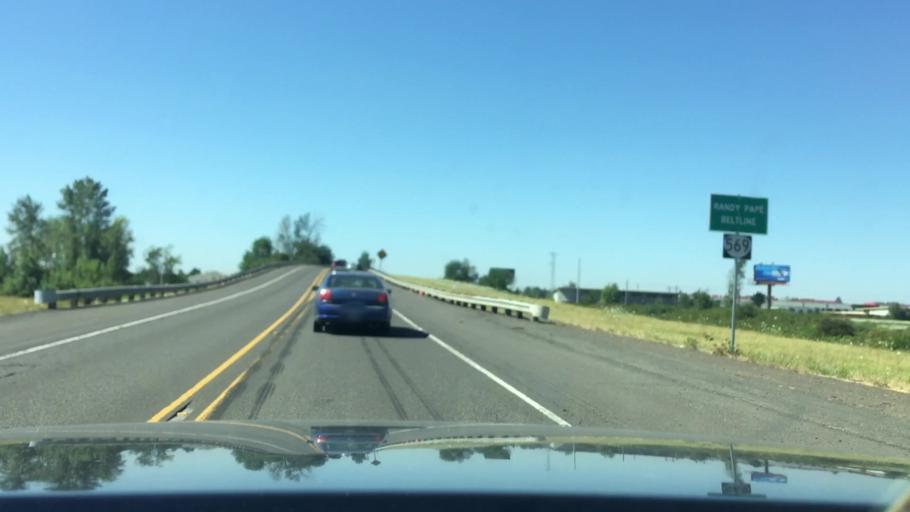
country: US
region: Oregon
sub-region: Lane County
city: Eugene
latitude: 44.0576
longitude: -123.1731
